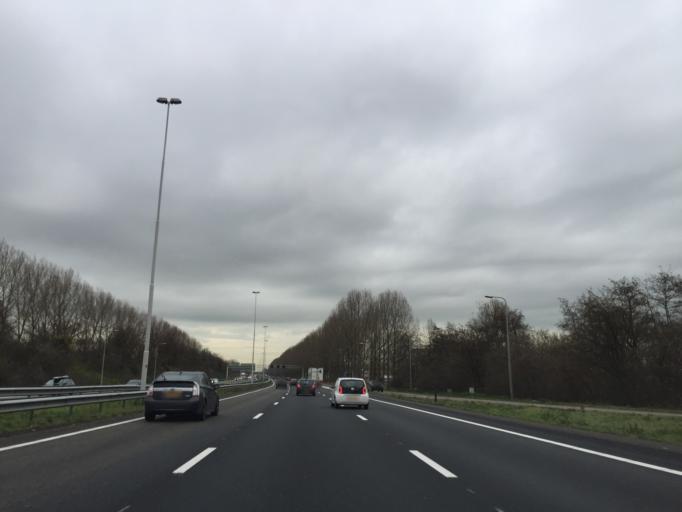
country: NL
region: South Holland
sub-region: Gemeente Capelle aan den IJssel
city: Capelle aan den IJssel
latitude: 51.9577
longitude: 4.5691
